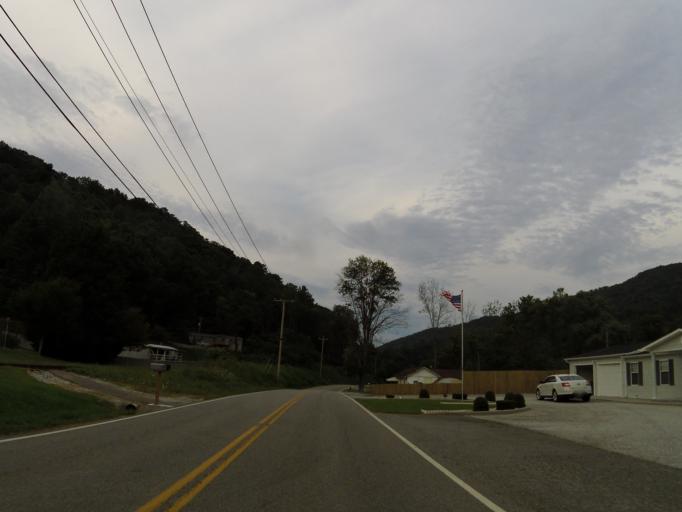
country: US
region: Tennessee
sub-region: Anderson County
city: Rocky Top
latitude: 36.2011
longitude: -84.1697
